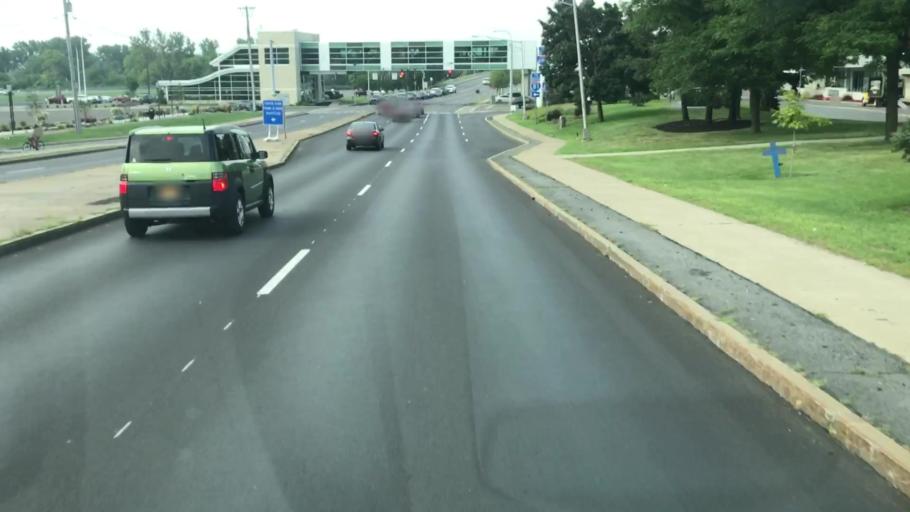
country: US
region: New York
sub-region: Onondaga County
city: Galeville
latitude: 43.0680
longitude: -76.1698
